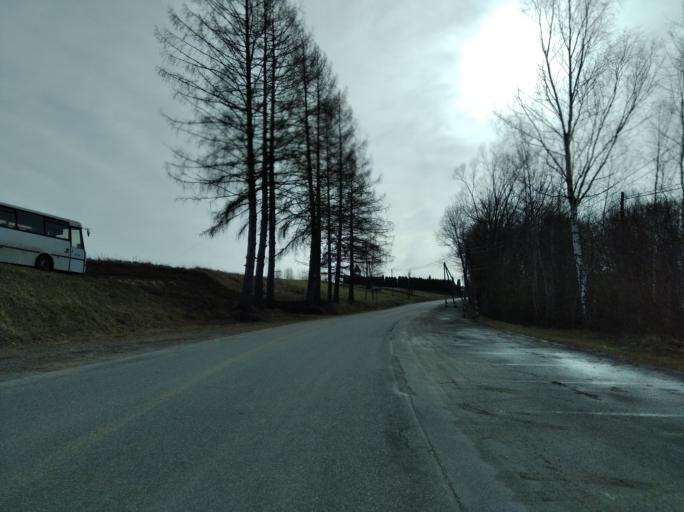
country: PL
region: Subcarpathian Voivodeship
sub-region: Powiat brzozowski
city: Jasienica Rosielna
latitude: 49.7478
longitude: 21.9416
